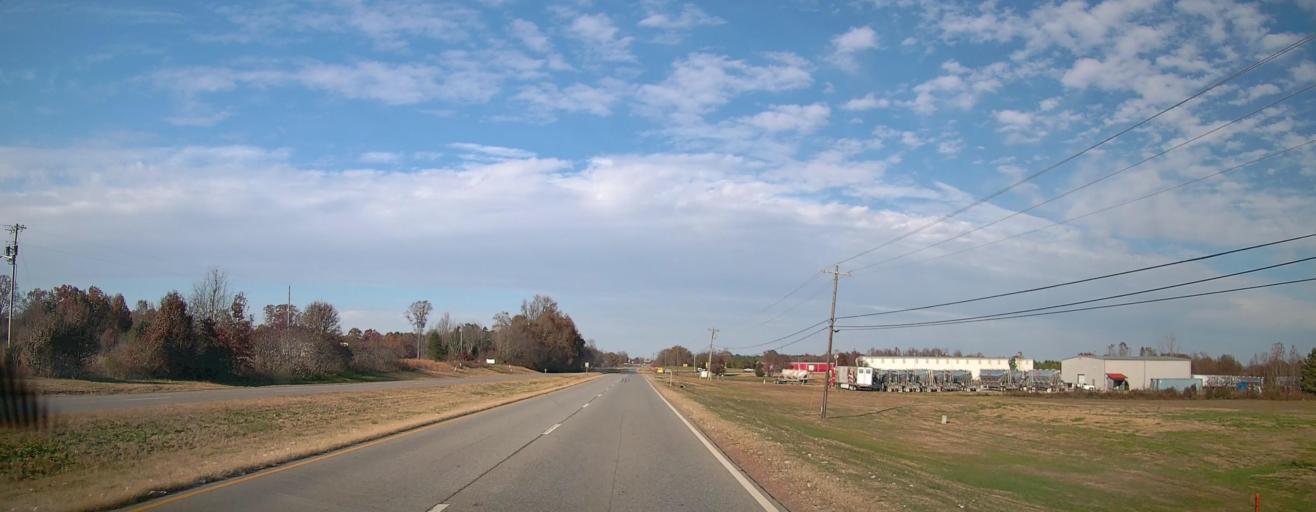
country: US
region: Alabama
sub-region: Limestone County
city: Athens
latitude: 34.7172
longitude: -86.9564
